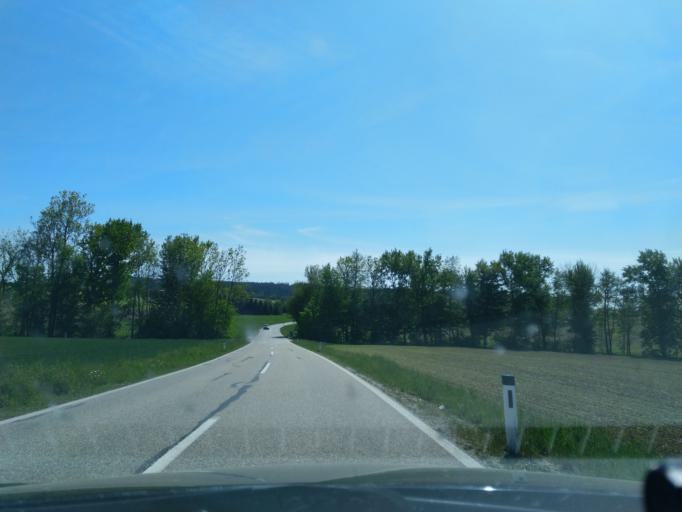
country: DE
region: Bavaria
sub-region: Lower Bavaria
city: Bad Fussing
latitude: 48.2720
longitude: 13.3534
